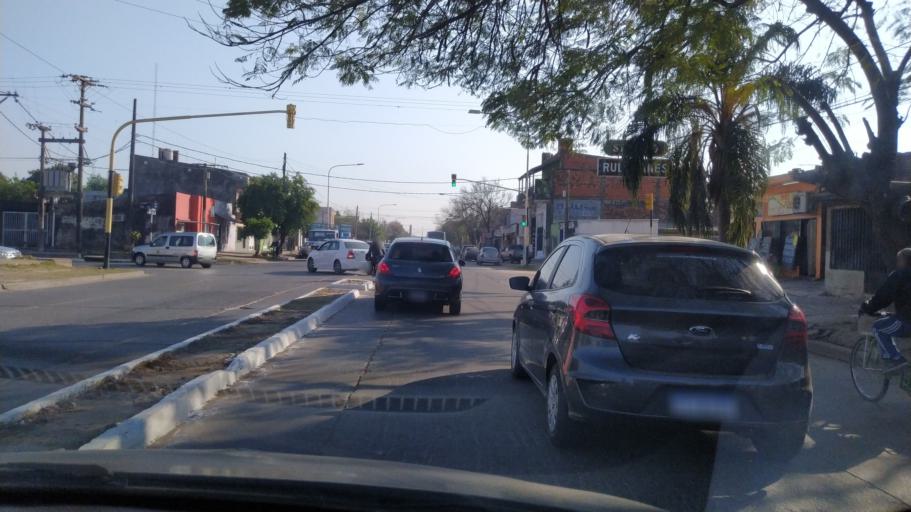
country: AR
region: Corrientes
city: Corrientes
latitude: -27.4834
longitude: -58.8156
